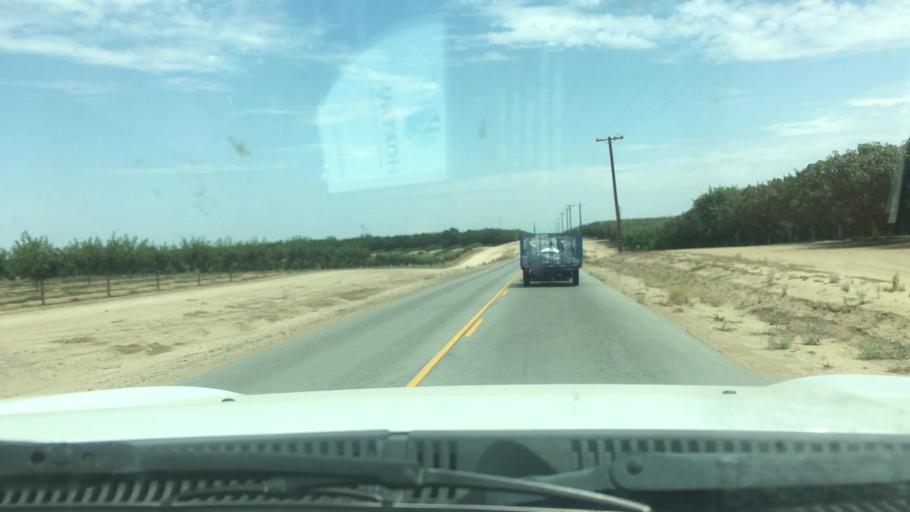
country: US
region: California
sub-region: Kern County
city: McFarland
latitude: 35.5924
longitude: -119.1510
